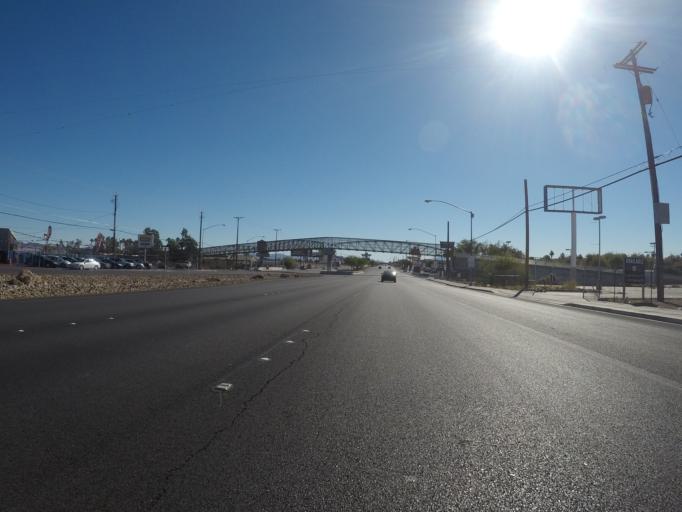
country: US
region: Nevada
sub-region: Clark County
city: Winchester
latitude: 36.1421
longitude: -115.0976
